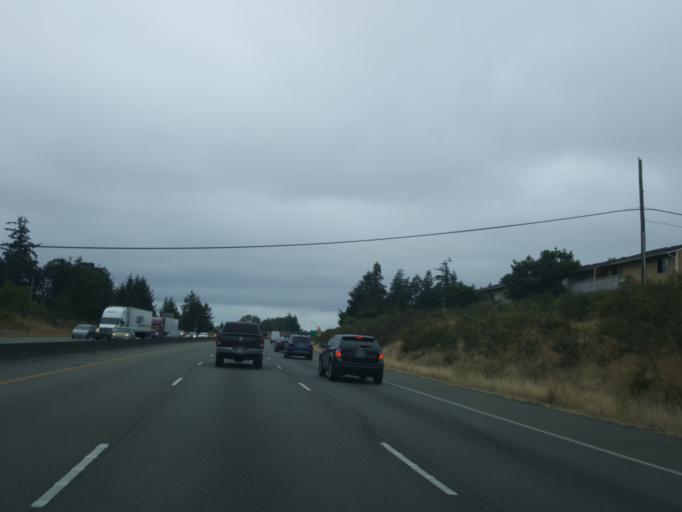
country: US
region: Washington
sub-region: Pierce County
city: Parkland
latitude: 47.1586
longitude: -122.4593
